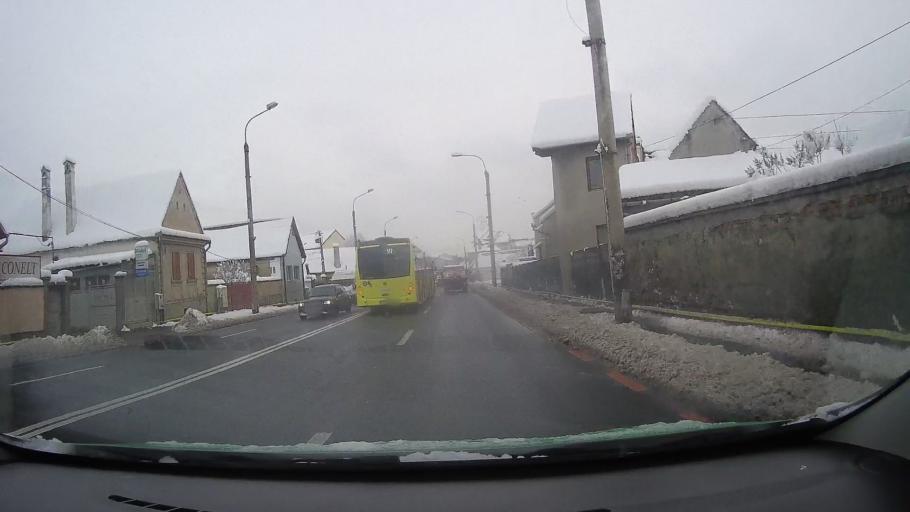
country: RO
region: Sibiu
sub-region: Municipiul Sibiu
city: Sibiu
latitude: 45.7935
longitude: 24.1175
